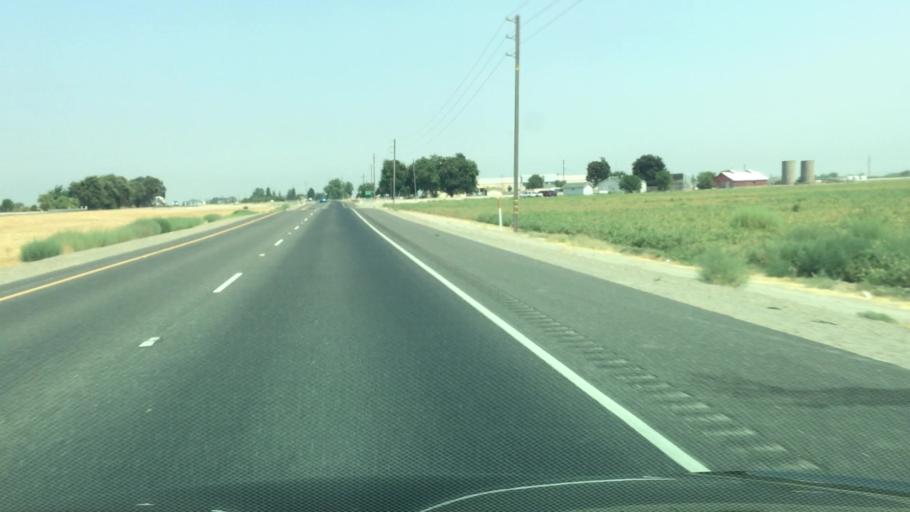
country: US
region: California
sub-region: Merced County
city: Dos Palos
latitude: 37.0475
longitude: -120.6001
